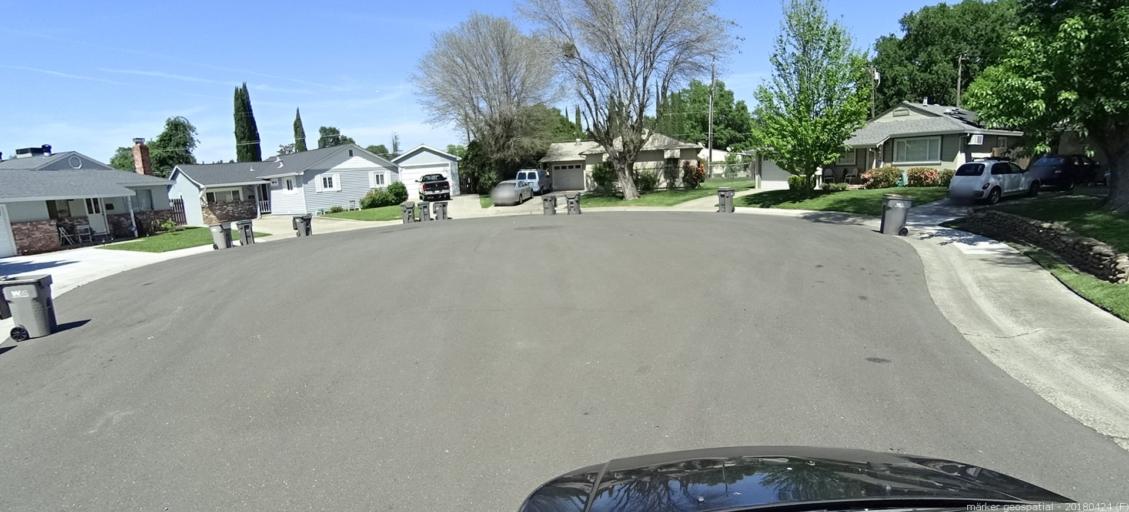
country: US
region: California
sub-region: Yolo County
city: West Sacramento
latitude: 38.5841
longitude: -121.5276
